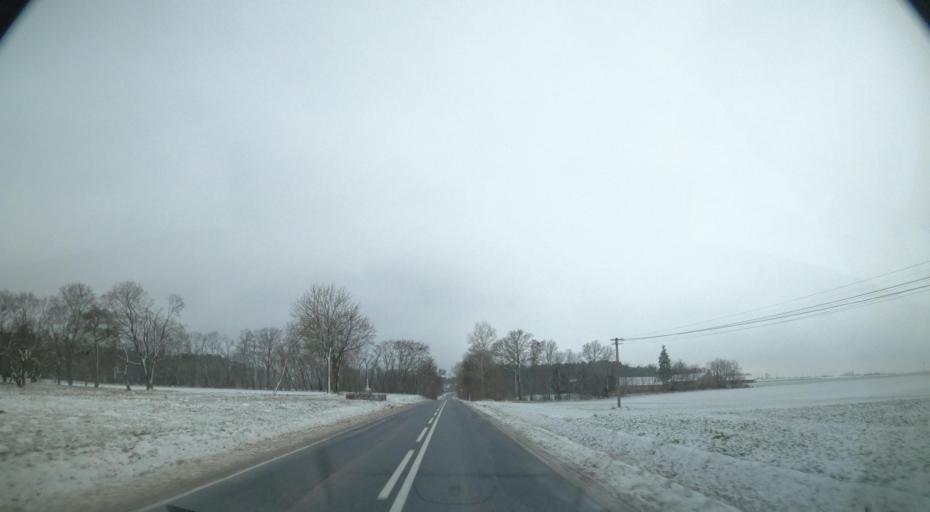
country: PL
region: Masovian Voivodeship
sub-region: Powiat plocki
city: Nowy Duninow
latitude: 52.6084
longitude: 19.4789
